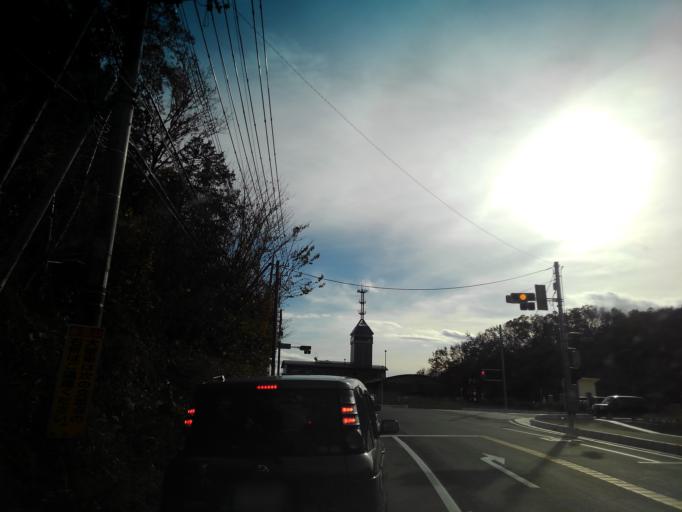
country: JP
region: Saitama
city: Hanno
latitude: 35.8713
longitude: 139.3340
